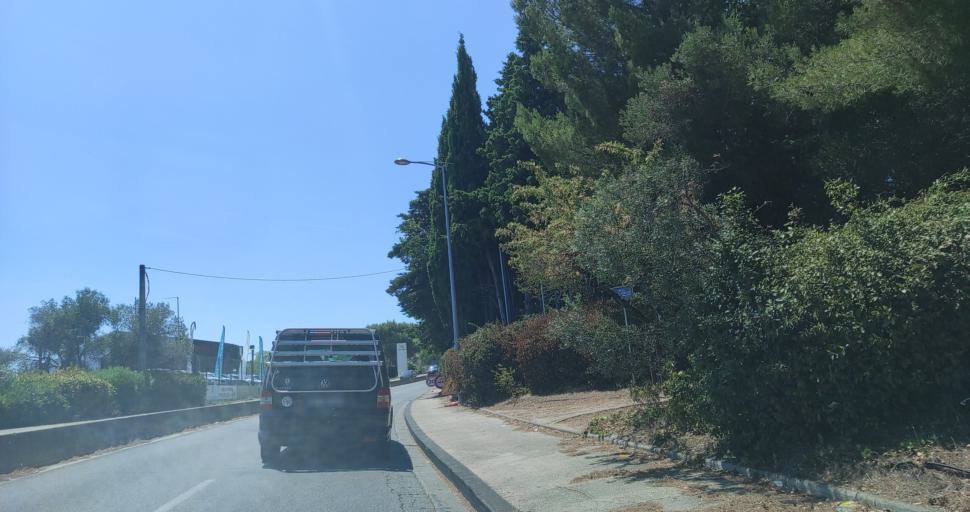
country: FR
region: Provence-Alpes-Cote d'Azur
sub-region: Departement des Bouches-du-Rhone
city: Martigues
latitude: 43.4216
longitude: 5.0569
